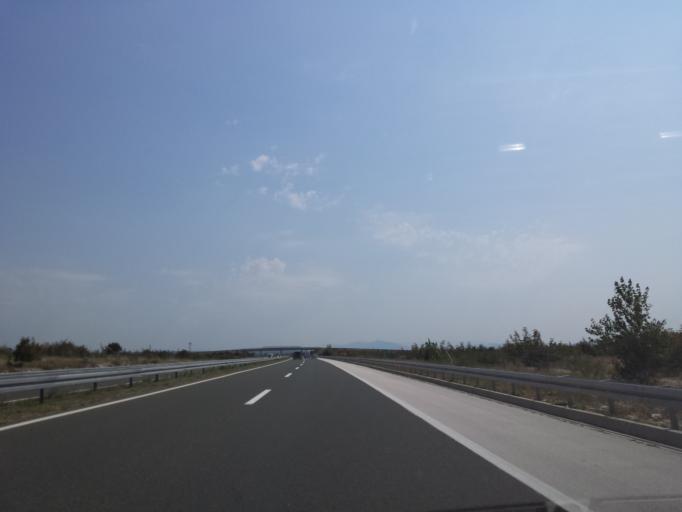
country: HR
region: Sibensko-Kniniska
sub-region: Grad Sibenik
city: Pirovac
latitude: 43.9097
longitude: 15.7541
